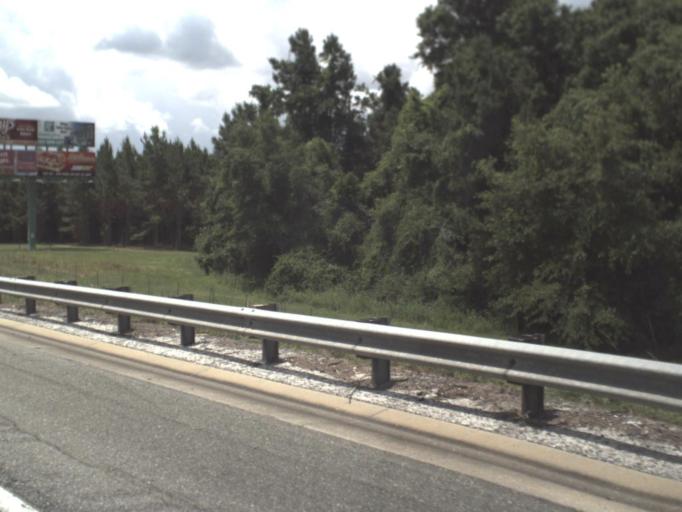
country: US
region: Florida
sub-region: Columbia County
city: Lake City
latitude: 30.2032
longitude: -82.7007
